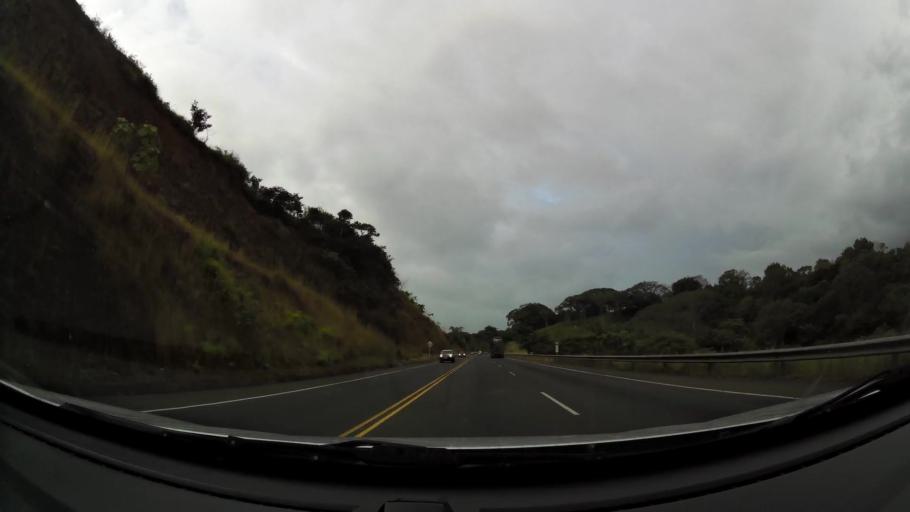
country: CR
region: Alajuela
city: Atenas
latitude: 9.9655
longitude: -84.3386
